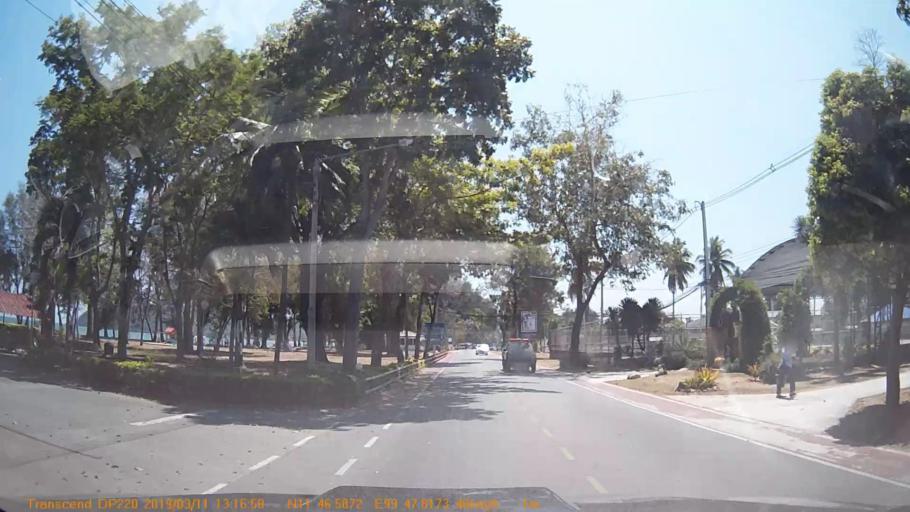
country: TH
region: Prachuap Khiri Khan
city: Prachuap Khiri Khan
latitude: 11.7763
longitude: 99.7969
